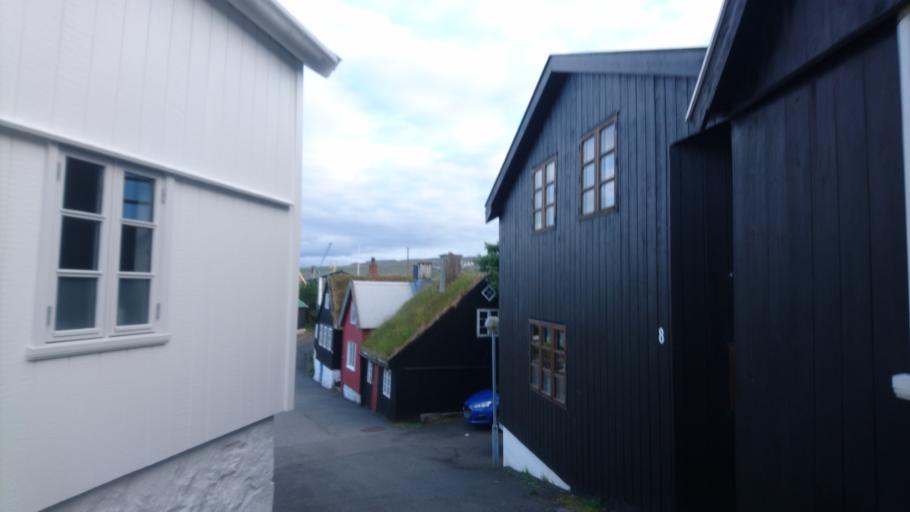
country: FO
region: Streymoy
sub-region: Torshavn
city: Torshavn
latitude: 62.0090
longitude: -6.7704
